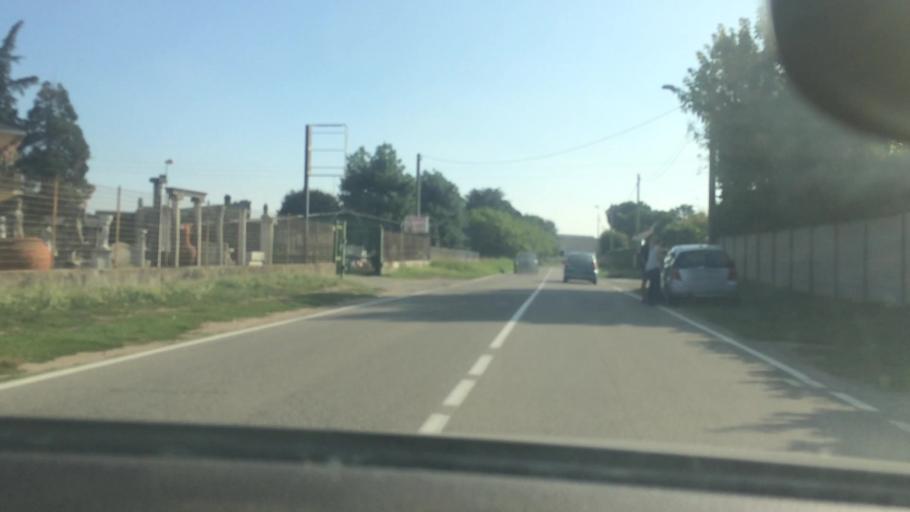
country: IT
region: Lombardy
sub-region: Citta metropolitana di Milano
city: Busto Garolfo
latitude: 45.5371
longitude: 8.8740
